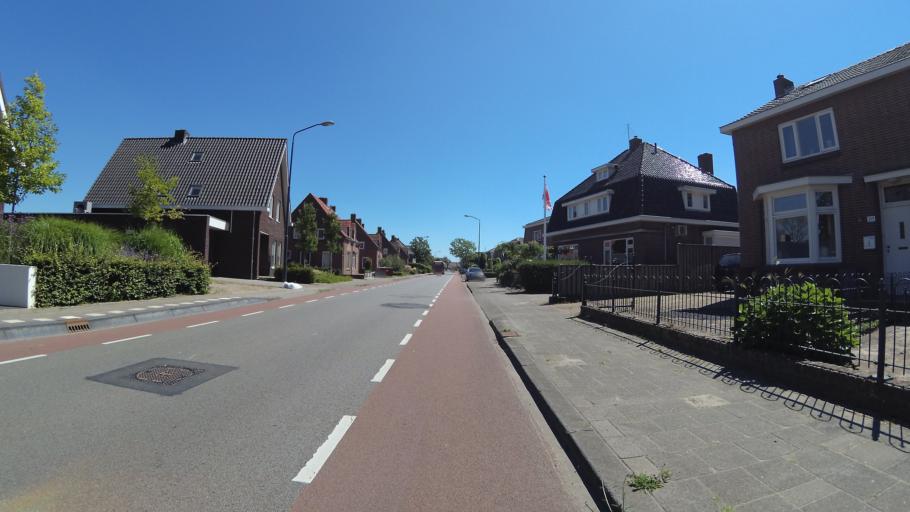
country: NL
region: North Brabant
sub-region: Gemeente Waalwijk
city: Waspik
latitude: 51.6784
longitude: 4.9907
